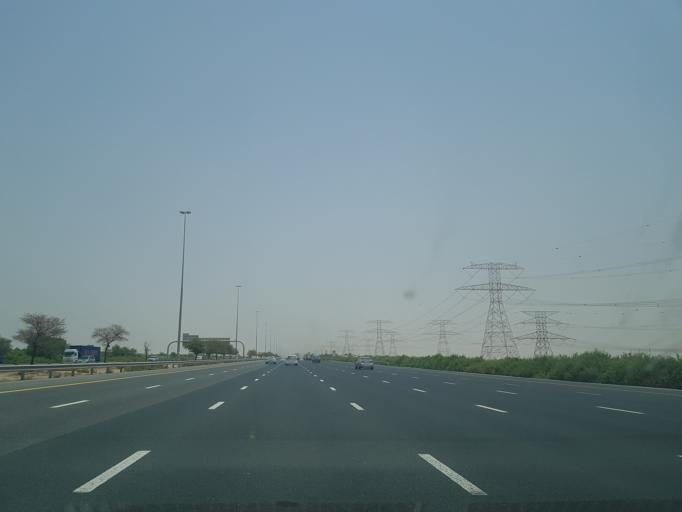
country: AE
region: Dubai
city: Dubai
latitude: 25.0950
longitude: 55.4042
